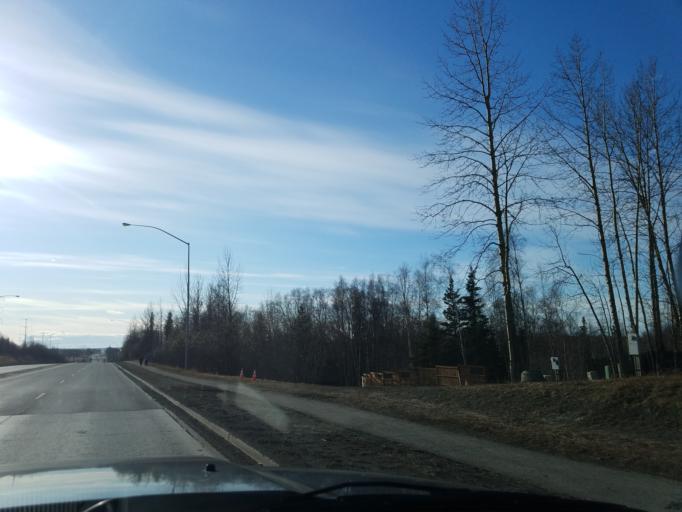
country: US
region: Alaska
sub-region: Anchorage Municipality
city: Elmendorf Air Force Base
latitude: 61.1808
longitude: -149.7537
